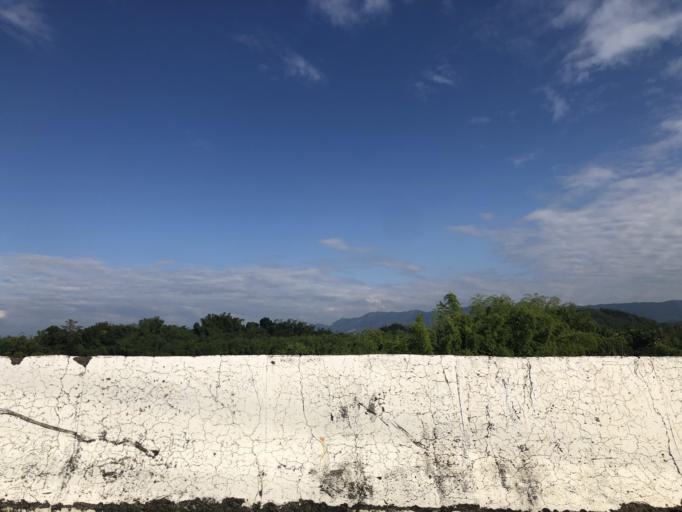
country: TW
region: Taiwan
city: Yujing
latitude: 23.0498
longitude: 120.4018
